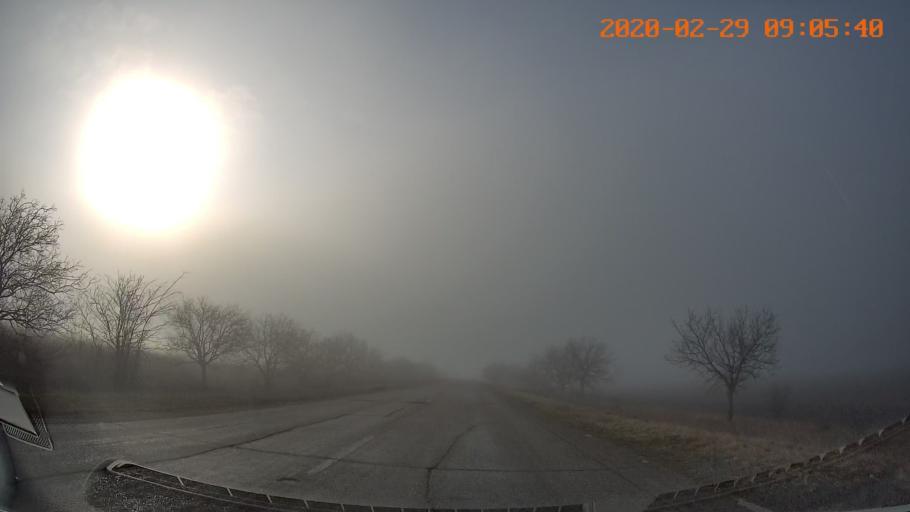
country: MD
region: Telenesti
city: Tiraspolul Nou
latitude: 46.8862
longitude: 29.7412
